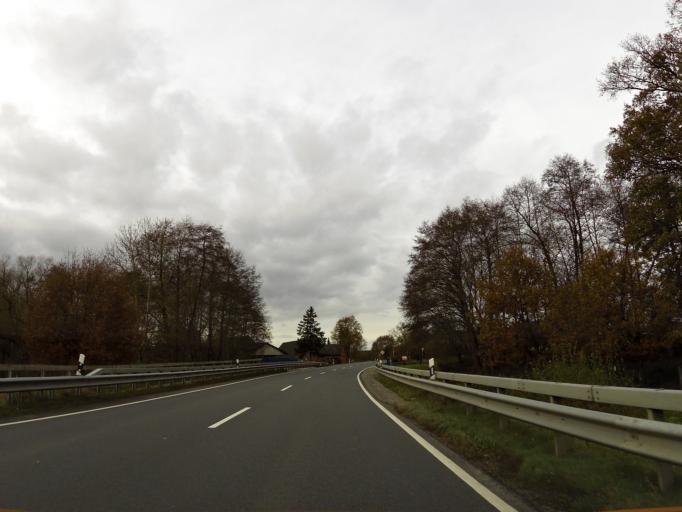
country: DE
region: Lower Saxony
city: Bergen an der Dumme
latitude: 52.8998
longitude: 10.9298
